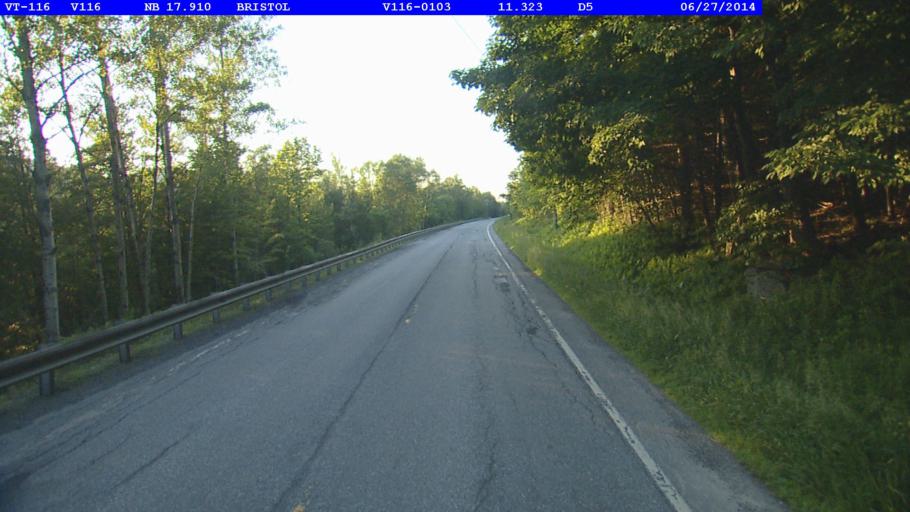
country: US
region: Vermont
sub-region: Addison County
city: Bristol
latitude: 44.1721
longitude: -73.0566
